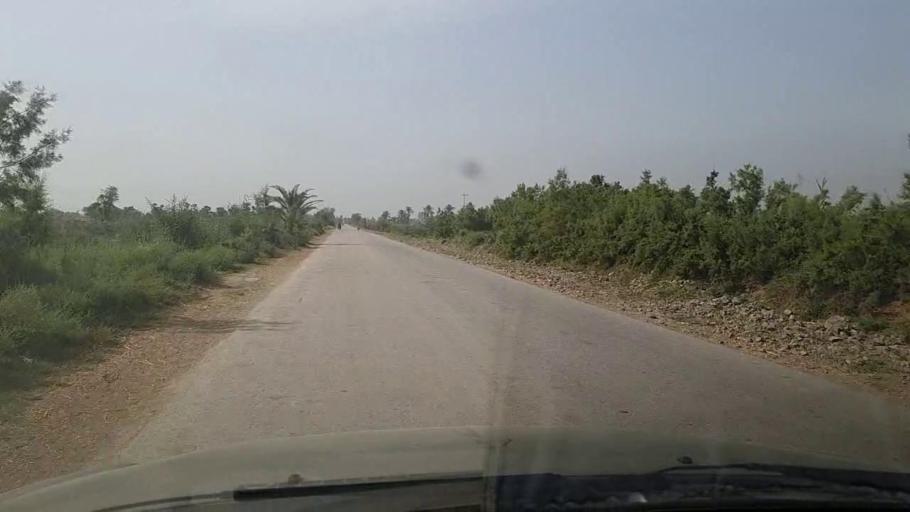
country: PK
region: Sindh
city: Gambat
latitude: 27.4488
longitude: 68.4861
